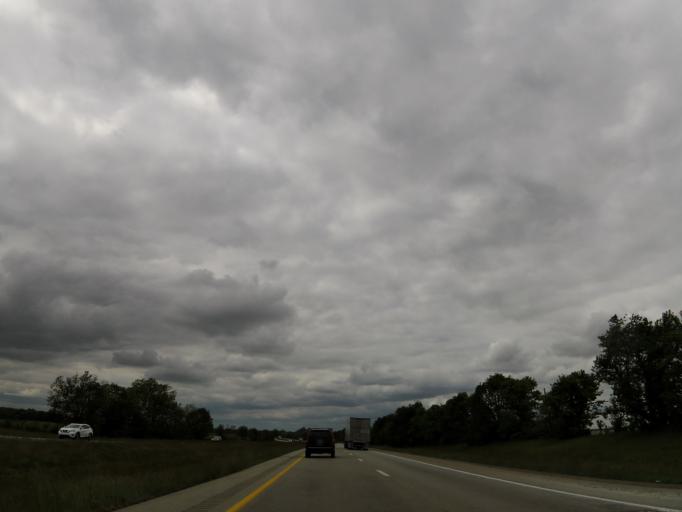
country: US
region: Kentucky
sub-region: Scott County
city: Georgetown
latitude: 38.1395
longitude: -84.5698
